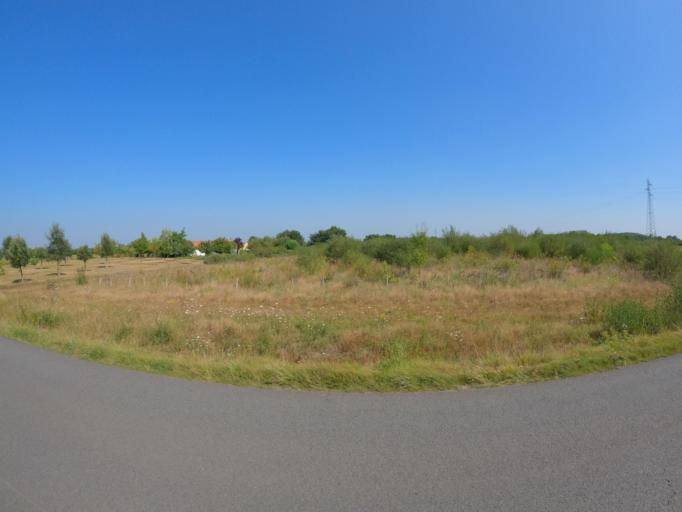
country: FR
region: Pays de la Loire
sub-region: Departement de la Loire-Atlantique
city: Pont-Saint-Martin
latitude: 47.1190
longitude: -1.5619
